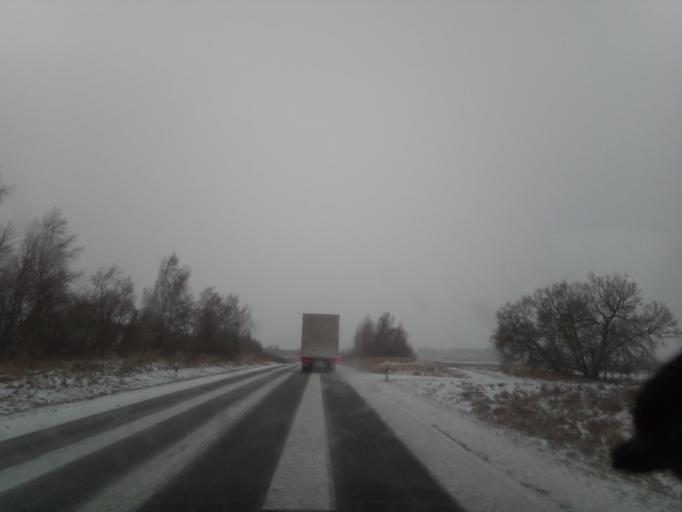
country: LT
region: Utenos apskritis
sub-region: Anyksciai
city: Anyksciai
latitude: 55.3886
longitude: 25.0592
